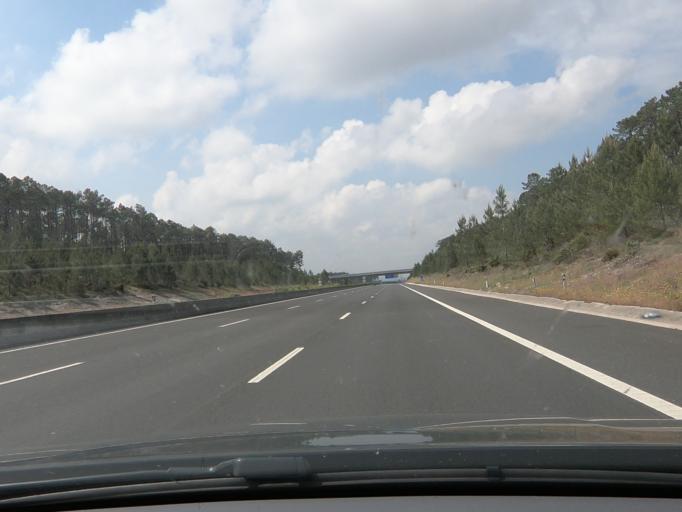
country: PT
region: Leiria
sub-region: Alcobaca
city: Pataias
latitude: 39.6468
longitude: -8.9655
